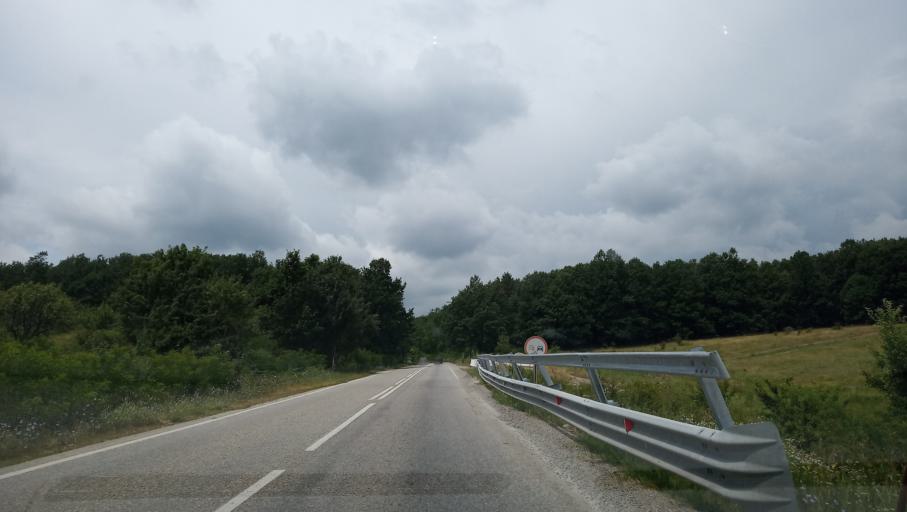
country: RO
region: Gorj
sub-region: Comuna Arcani
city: Arcani
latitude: 45.0896
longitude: 23.1232
